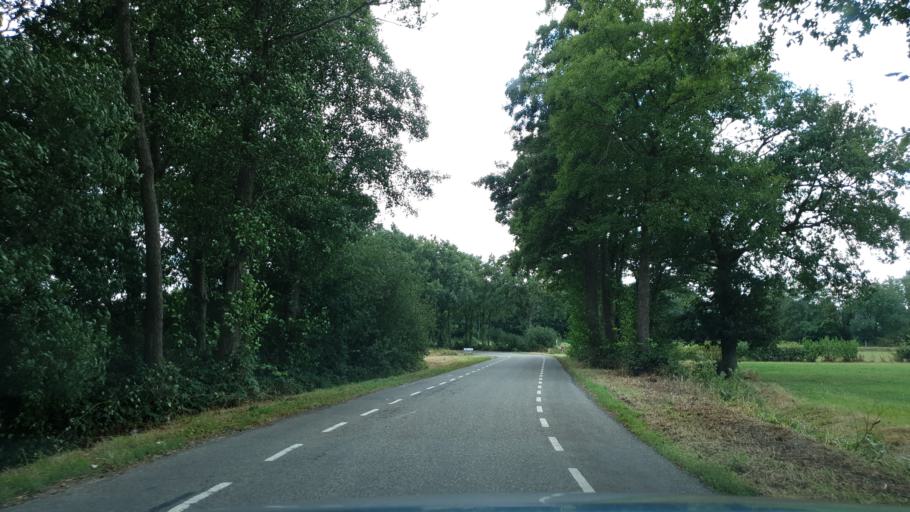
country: NL
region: Gelderland
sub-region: Gemeente Nijmegen
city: Lindenholt
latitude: 51.7718
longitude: 5.8086
